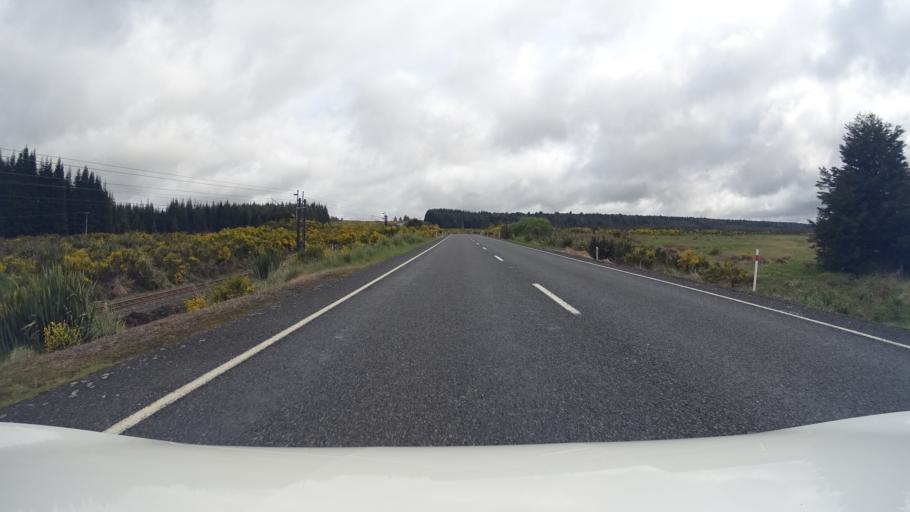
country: NZ
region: Manawatu-Wanganui
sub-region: Ruapehu District
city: Waiouru
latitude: -39.2088
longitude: 175.4023
